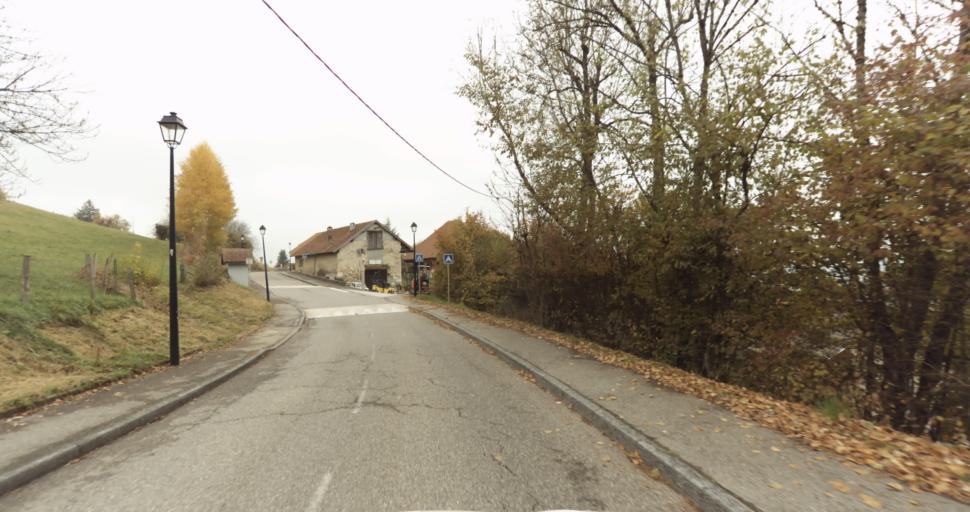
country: FR
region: Rhone-Alpes
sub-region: Departement de la Haute-Savoie
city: Viuz-la-Chiesaz
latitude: 45.8352
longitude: 6.0781
